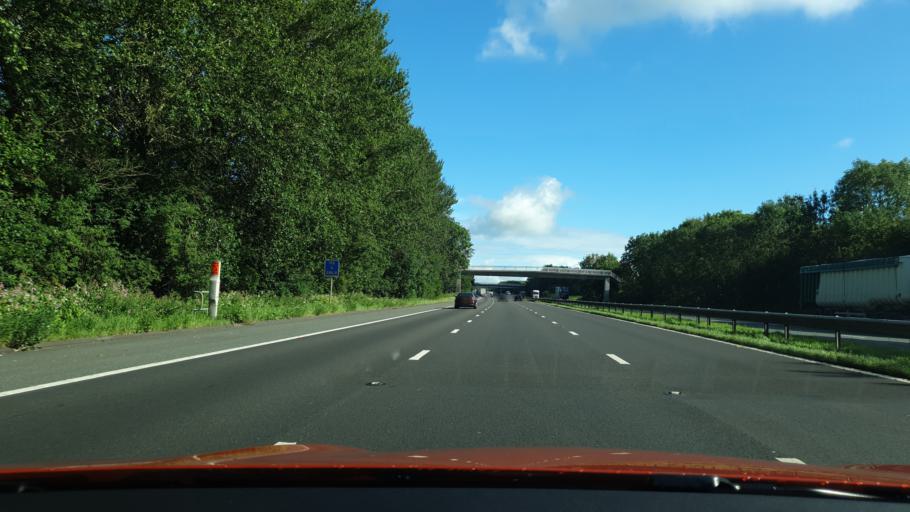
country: GB
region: England
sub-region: Lancashire
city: Carnforth
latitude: 54.1521
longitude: -2.7385
